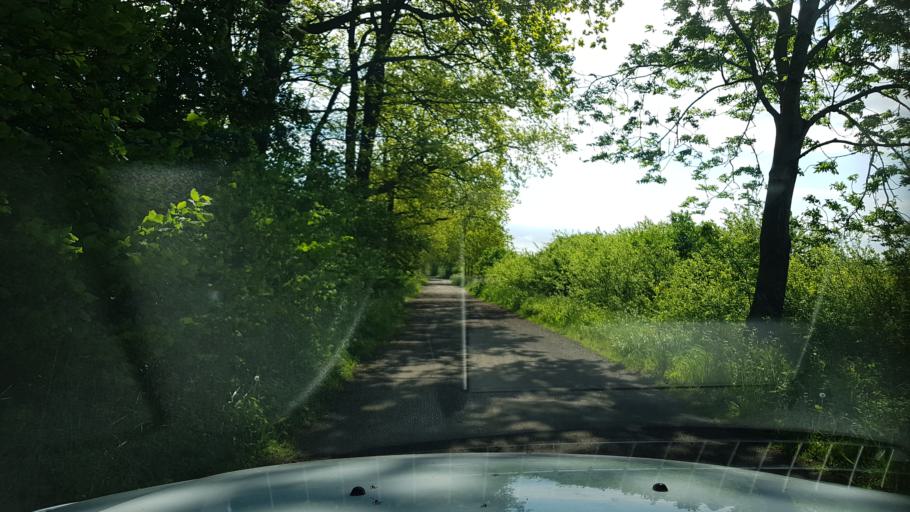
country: PL
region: West Pomeranian Voivodeship
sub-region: Powiat kolobrzeski
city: Ustronie Morskie
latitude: 54.2223
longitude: 15.8198
